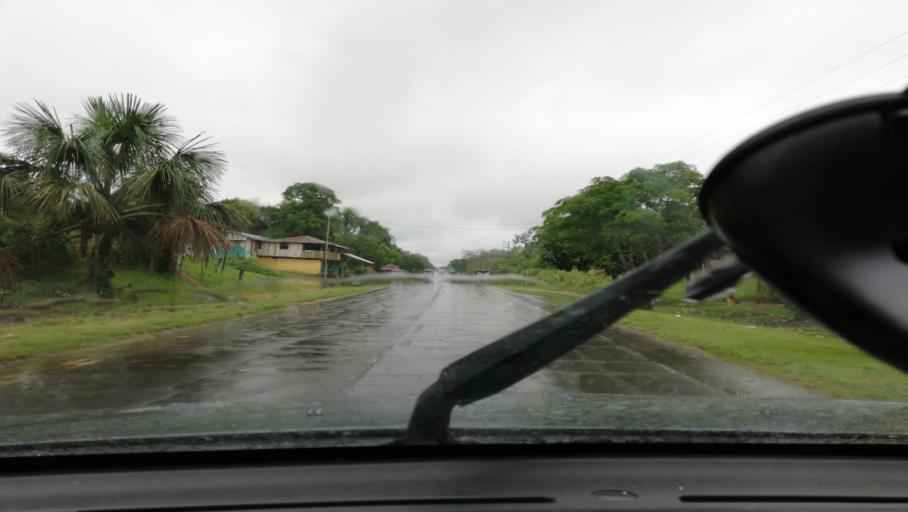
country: PE
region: Loreto
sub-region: Provincia de Maynas
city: San Juan
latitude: -4.0871
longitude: -73.4498
